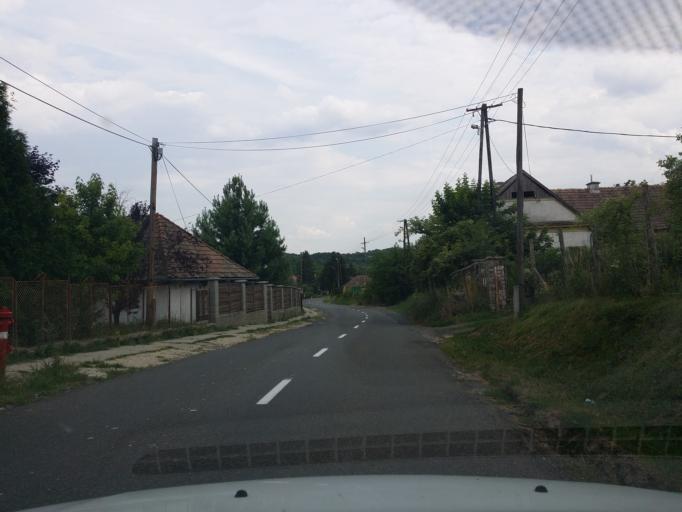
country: HU
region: Nograd
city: Bercel
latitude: 47.9127
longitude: 19.3752
